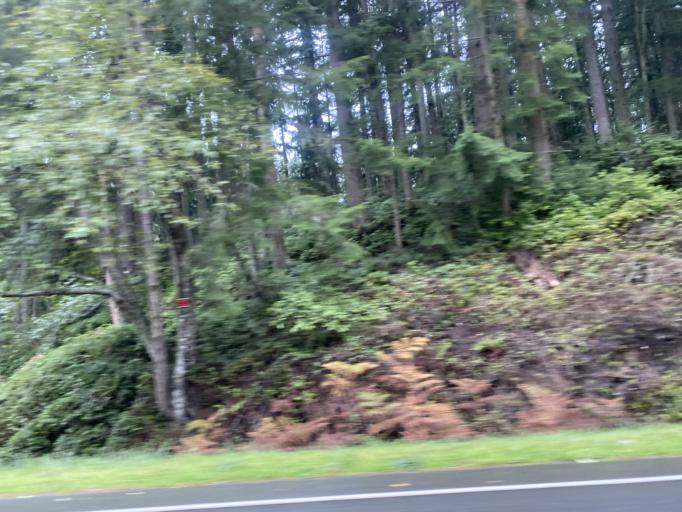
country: US
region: Washington
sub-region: Island County
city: Langley
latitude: 48.0487
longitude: -122.4464
